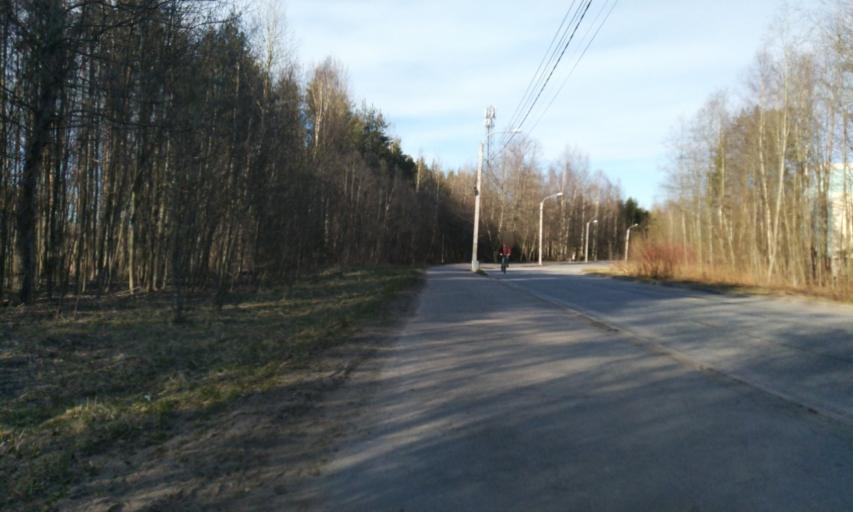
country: RU
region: Leningrad
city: Toksovo
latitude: 60.1165
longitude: 30.4880
